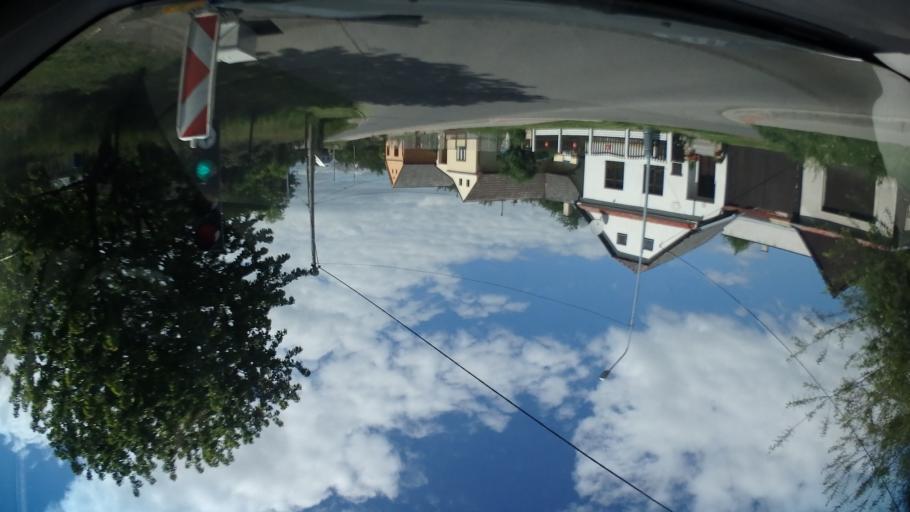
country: CZ
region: Pardubicky
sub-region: Okres Svitavy
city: Moravska Trebova
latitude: 49.7640
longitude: 16.6502
